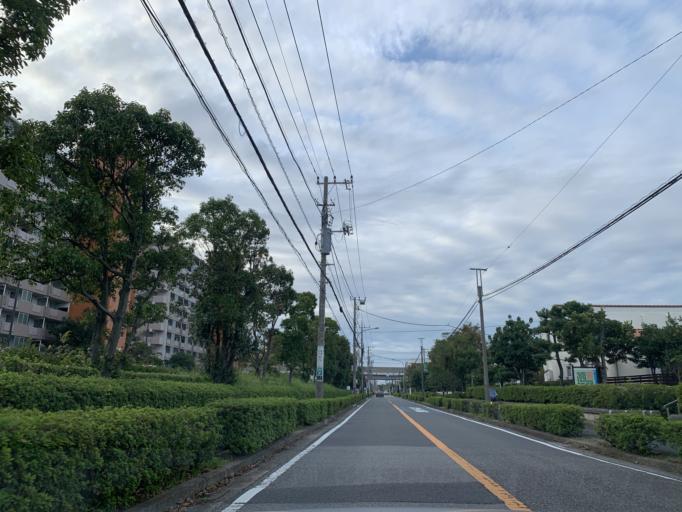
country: JP
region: Tokyo
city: Urayasu
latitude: 35.6516
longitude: 139.9181
